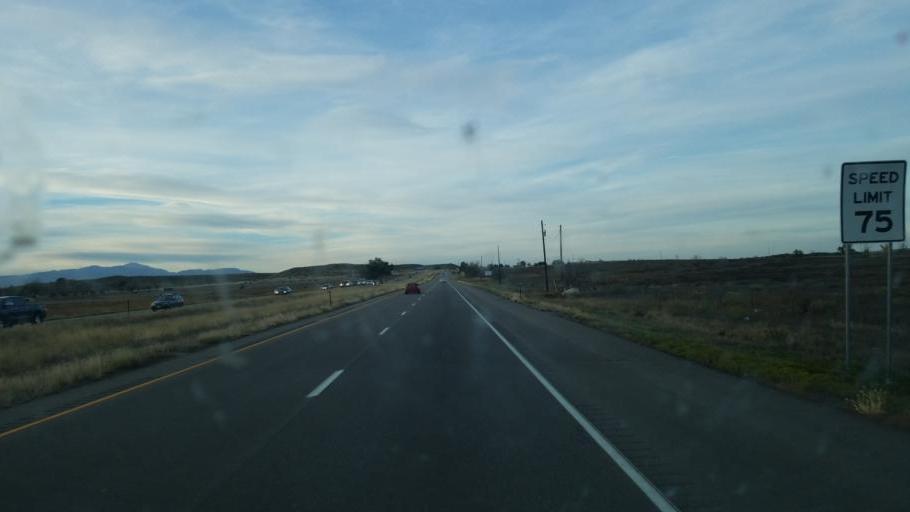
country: US
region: Colorado
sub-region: Pueblo County
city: Pueblo West
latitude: 38.4916
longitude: -104.6225
